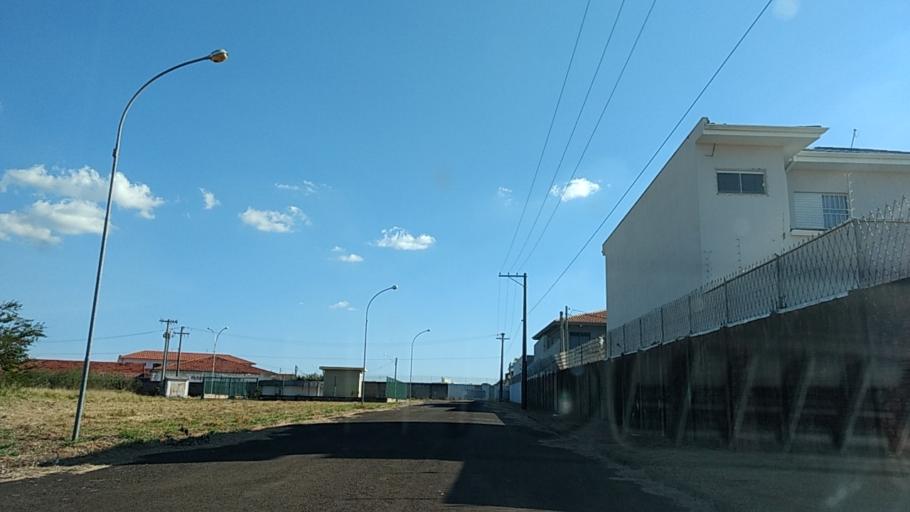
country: BR
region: Sao Paulo
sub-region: Botucatu
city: Botucatu
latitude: -22.8542
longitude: -48.4365
